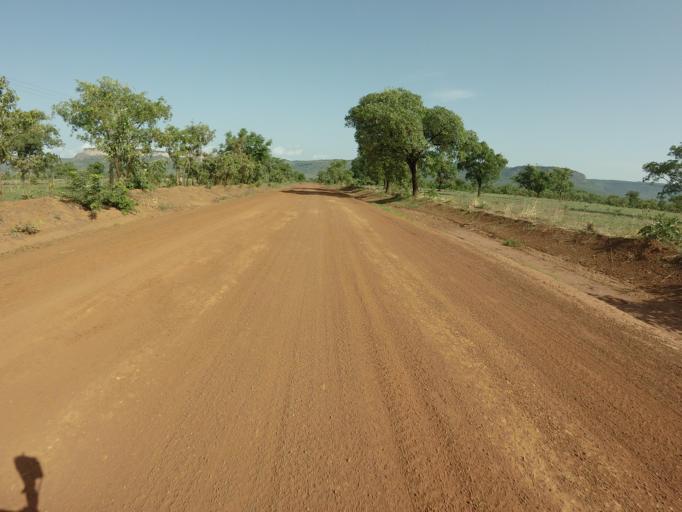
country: GH
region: Upper East
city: Bawku
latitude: 10.6805
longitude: -0.2135
